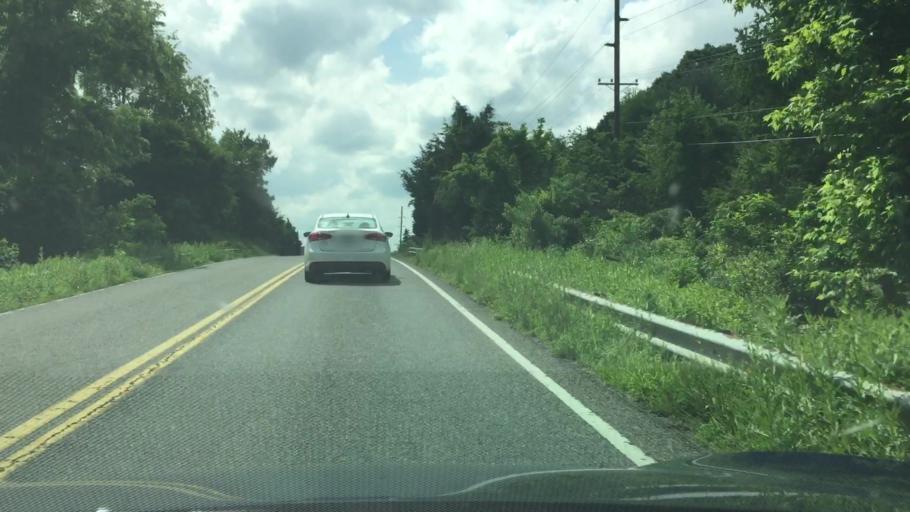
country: US
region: Virginia
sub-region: Pulaski County
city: Dublin
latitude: 37.0801
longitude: -80.6744
